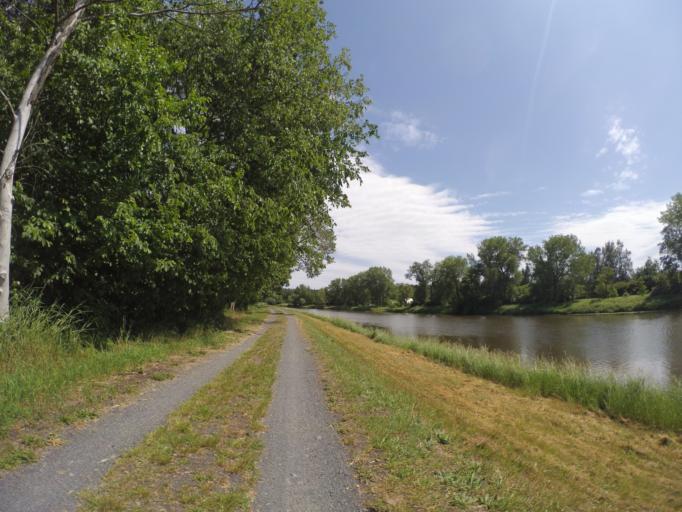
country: CZ
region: Central Bohemia
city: Poricany
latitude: 50.1665
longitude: 14.9104
